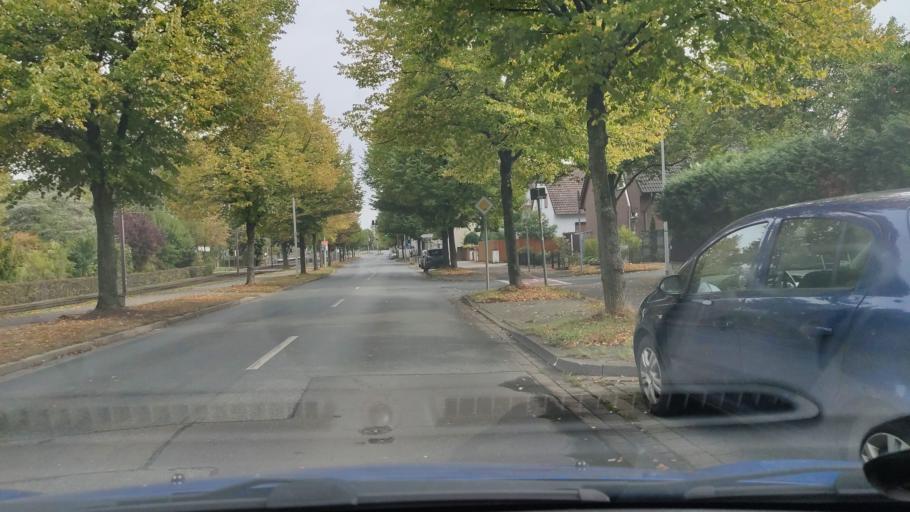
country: DE
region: Lower Saxony
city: Ronnenberg
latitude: 52.3771
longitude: 9.6706
